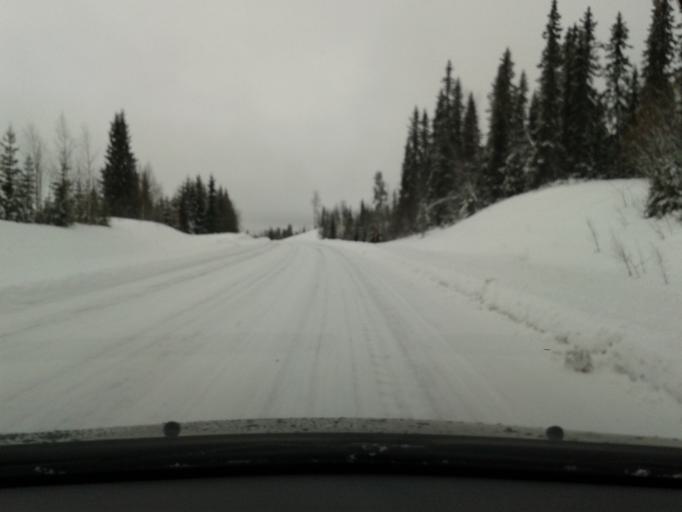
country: SE
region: Vaesterbotten
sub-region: Vilhelmina Kommun
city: Sjoberg
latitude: 64.8801
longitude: 15.8695
